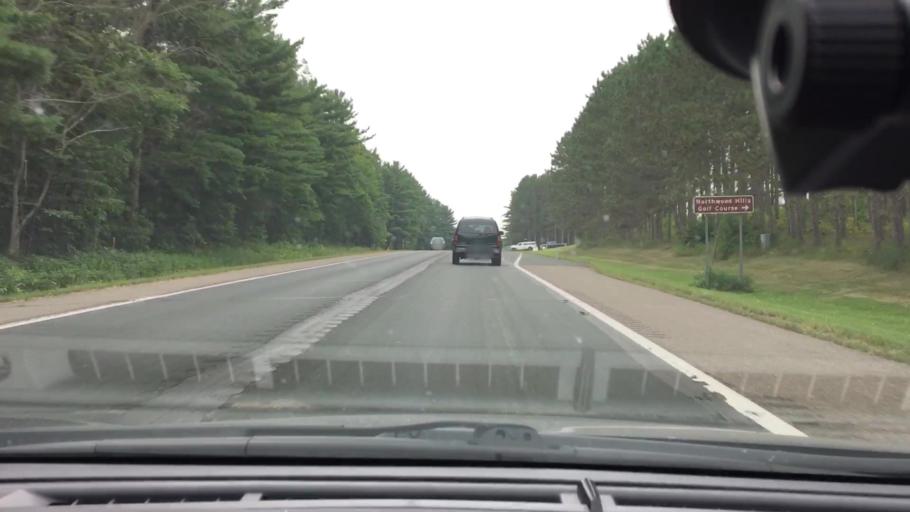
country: US
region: Minnesota
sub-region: Mille Lacs County
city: Vineland
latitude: 46.2267
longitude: -93.7928
